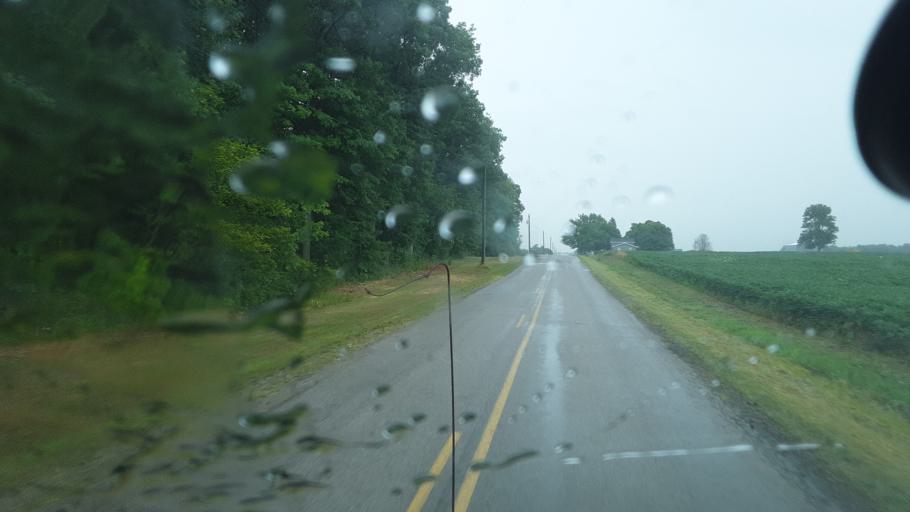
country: US
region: Indiana
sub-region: DeKalb County
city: Butler
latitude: 41.4536
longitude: -84.8137
